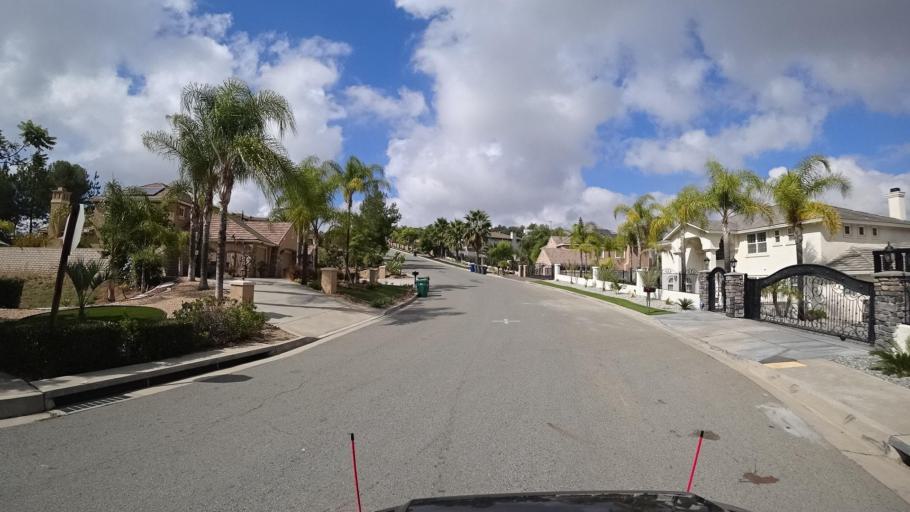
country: US
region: California
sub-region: San Diego County
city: Granite Hills
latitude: 32.7760
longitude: -116.9071
